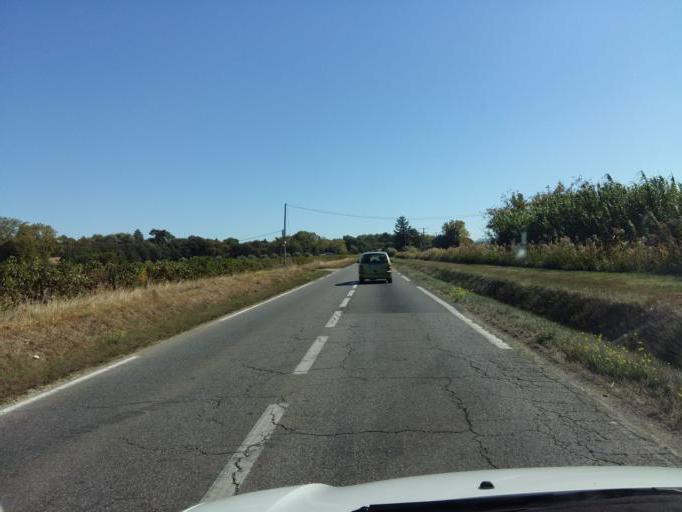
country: FR
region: Provence-Alpes-Cote d'Azur
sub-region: Departement du Vaucluse
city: Villelaure
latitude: 43.7036
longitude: 5.4483
